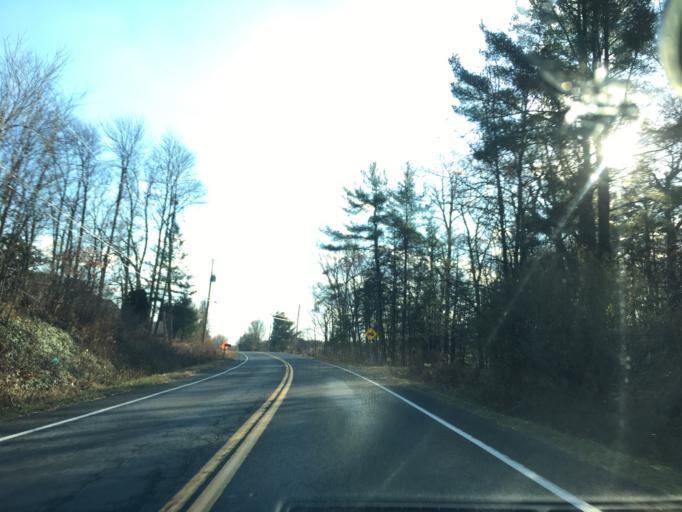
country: US
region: New York
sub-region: Rensselaer County
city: West Sand Lake
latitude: 42.6093
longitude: -73.6208
